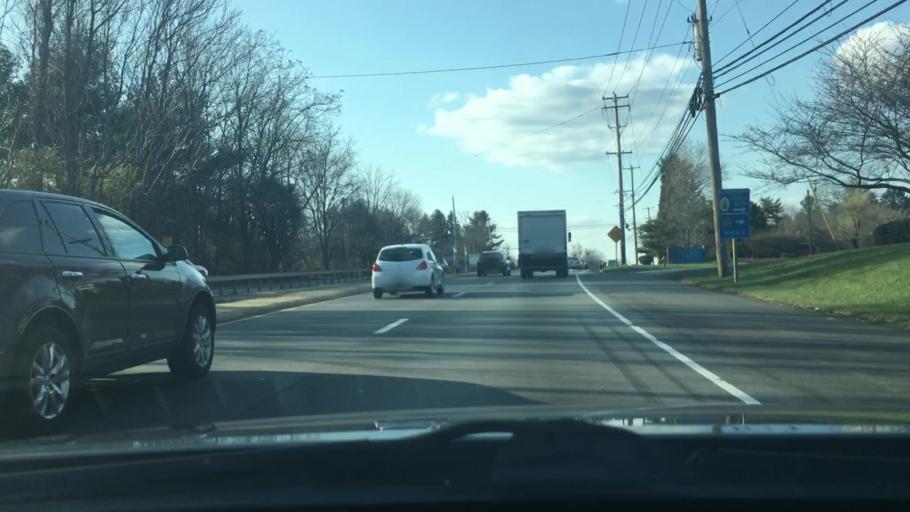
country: US
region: Pennsylvania
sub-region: Chester County
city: West Chester
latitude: 39.9320
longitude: -75.5869
